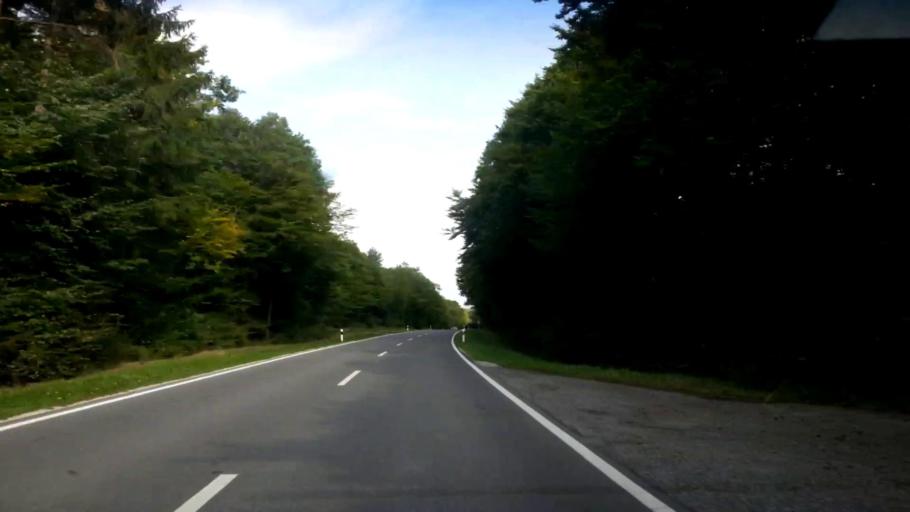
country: DE
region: Bavaria
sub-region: Regierungsbezirk Unterfranken
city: Eltmann
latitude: 49.9554
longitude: 10.6342
